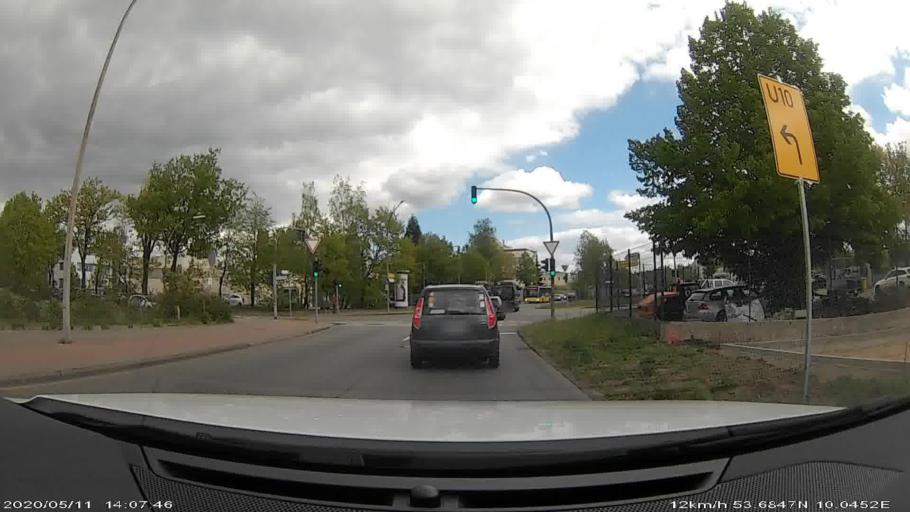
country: DE
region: Hamburg
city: Poppenbuettel
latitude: 53.6838
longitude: 10.0658
